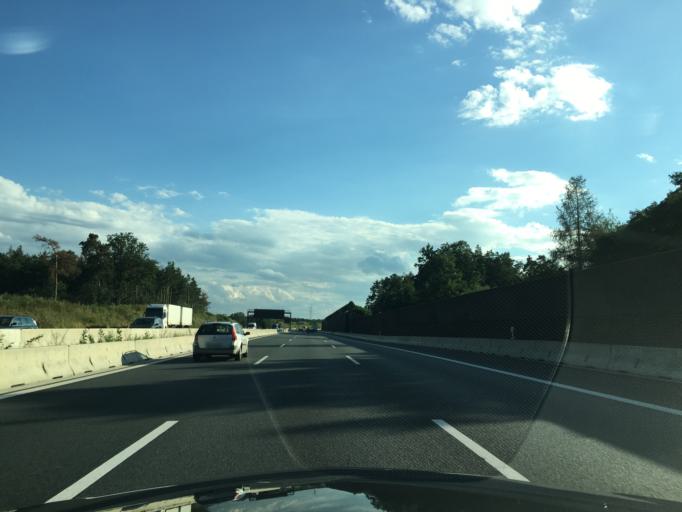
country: DE
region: Bavaria
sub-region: Regierungsbezirk Mittelfranken
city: Wendelstein
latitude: 49.3589
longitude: 11.1118
